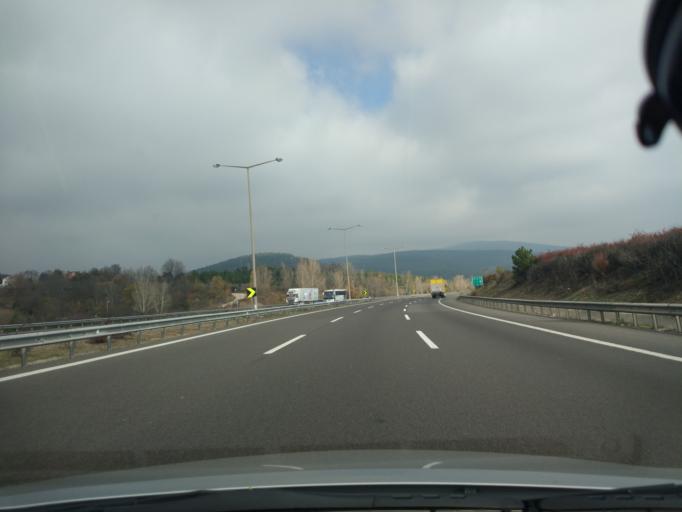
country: TR
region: Bolu
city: Bolu
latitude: 40.7487
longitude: 31.5620
